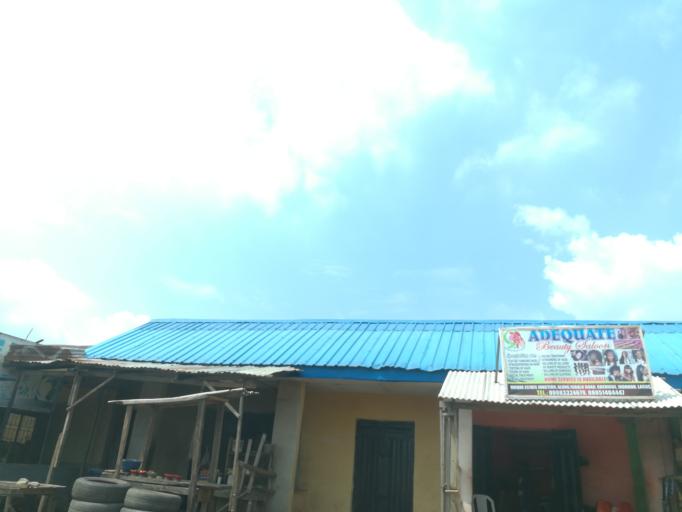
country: NG
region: Lagos
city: Ikorodu
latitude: 6.5920
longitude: 3.6432
